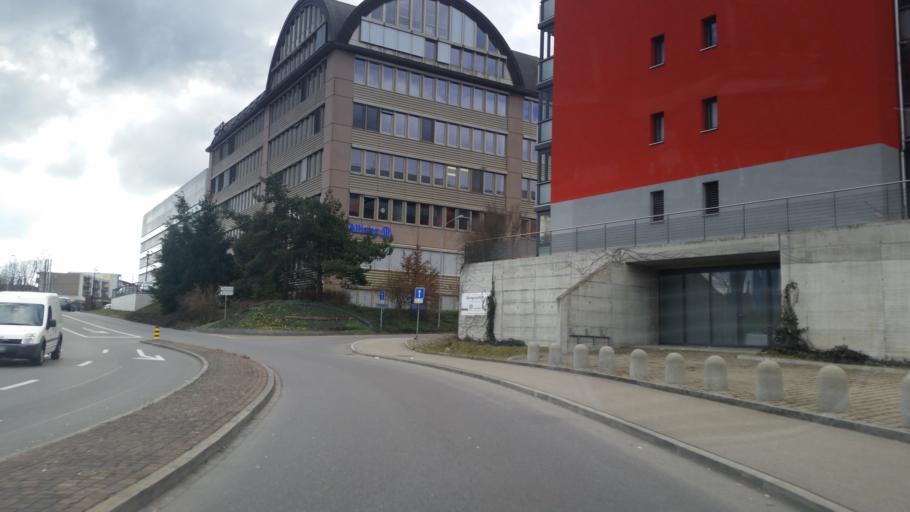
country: CH
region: Zurich
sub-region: Bezirk Dietikon
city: Dietikon / Vorstadt
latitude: 47.4083
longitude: 8.4025
